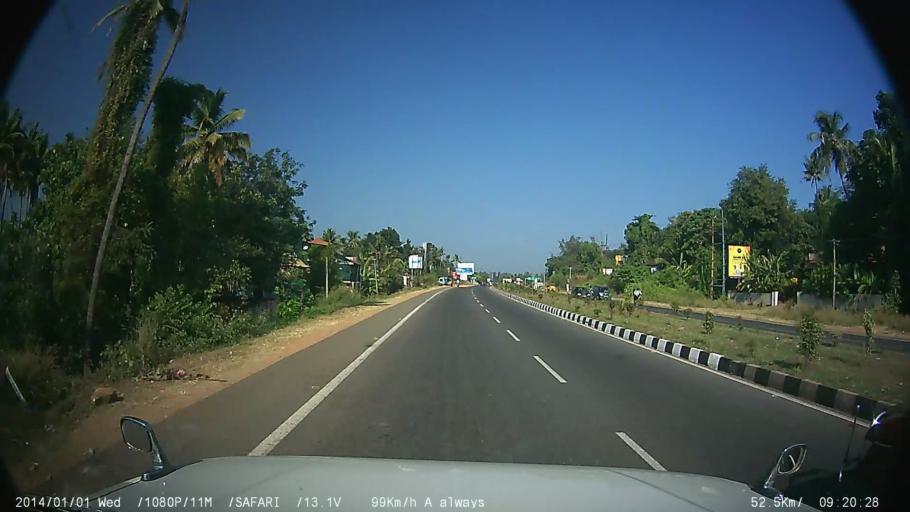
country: IN
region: Kerala
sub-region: Thrissur District
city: Kizhake Chalakudi
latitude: 10.2624
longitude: 76.3557
